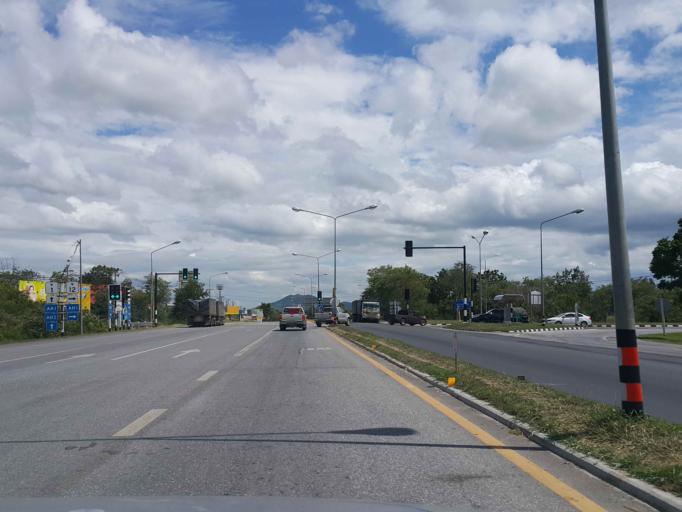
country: TH
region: Tak
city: Tak
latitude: 16.8422
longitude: 99.1134
